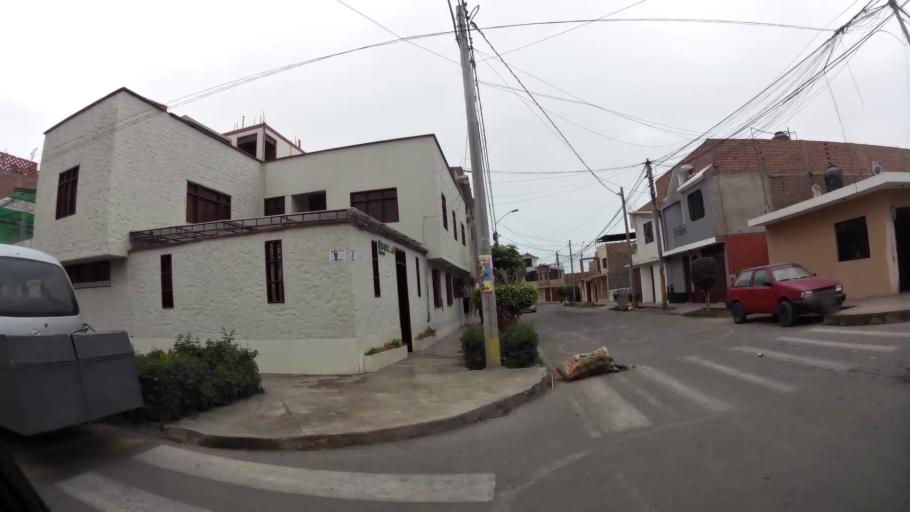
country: PE
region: Lima
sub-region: Barranca
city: Barranca
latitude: -10.7433
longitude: -77.7658
